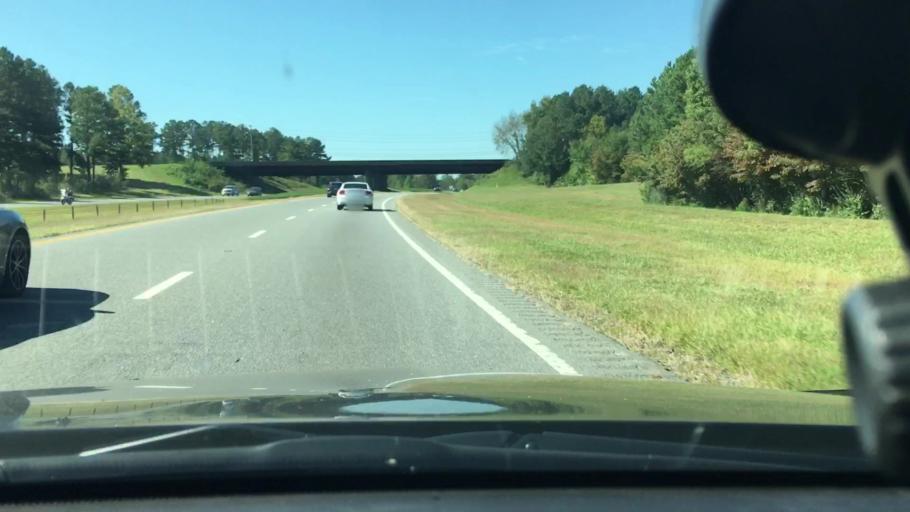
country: US
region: North Carolina
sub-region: Cleveland County
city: White Plains
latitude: 35.2482
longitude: -81.4054
